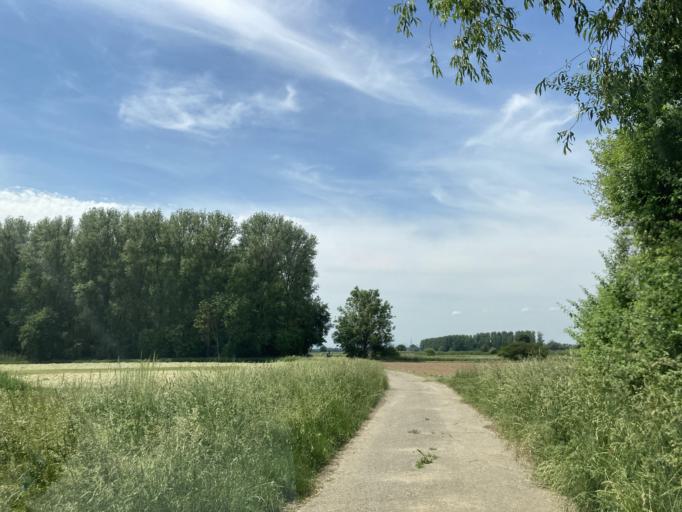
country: DE
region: Baden-Wuerttemberg
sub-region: Karlsruhe Region
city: Graben-Neudorf
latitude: 49.1727
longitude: 8.4658
